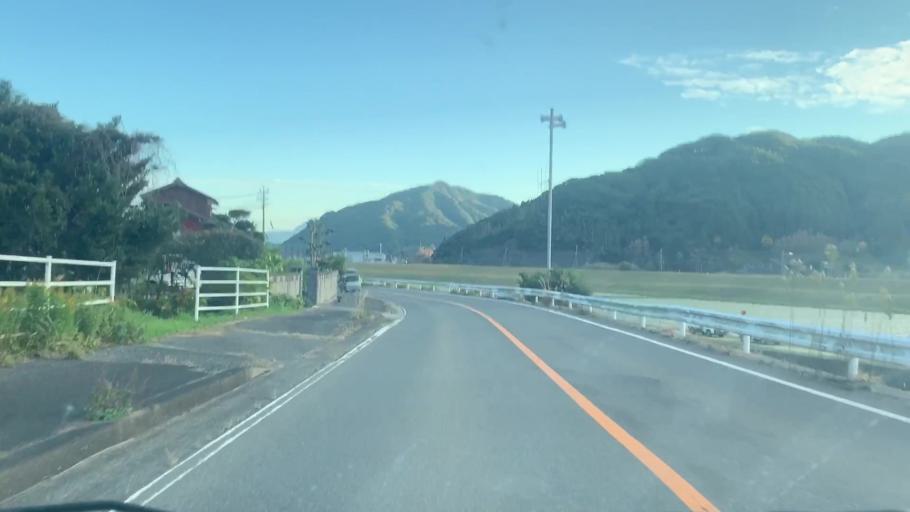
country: JP
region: Saga Prefecture
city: Karatsu
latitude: 33.3821
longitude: 129.9896
